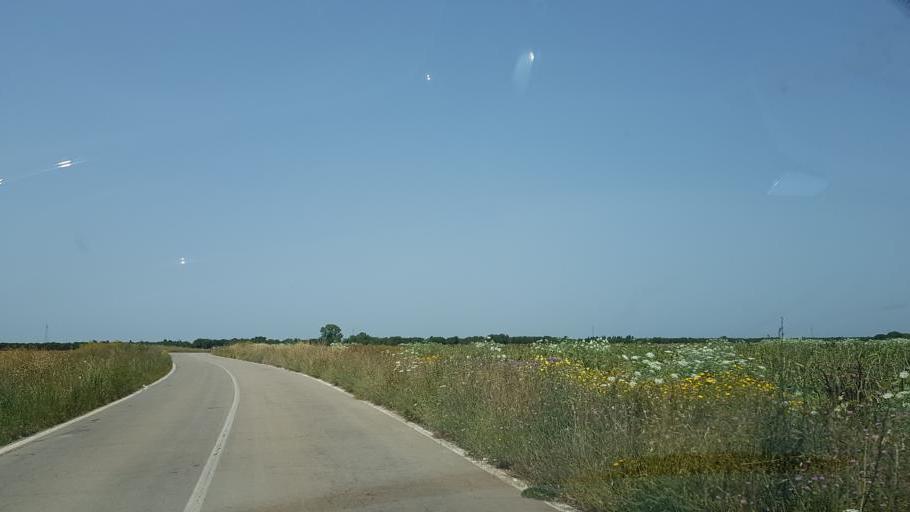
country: IT
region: Apulia
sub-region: Provincia di Brindisi
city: Mesagne
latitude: 40.5262
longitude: 17.8208
